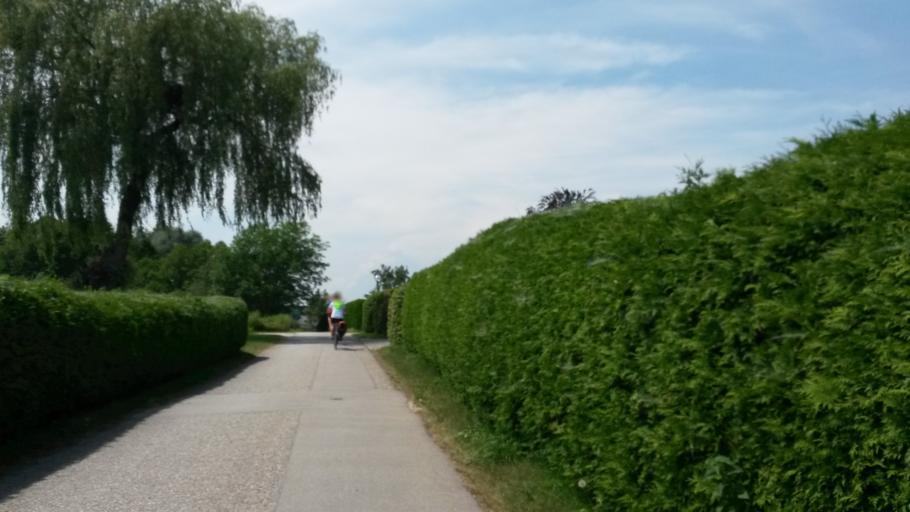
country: DE
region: Bavaria
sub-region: Upper Bavaria
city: Seeon-Seebruck
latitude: 47.9338
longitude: 12.4687
